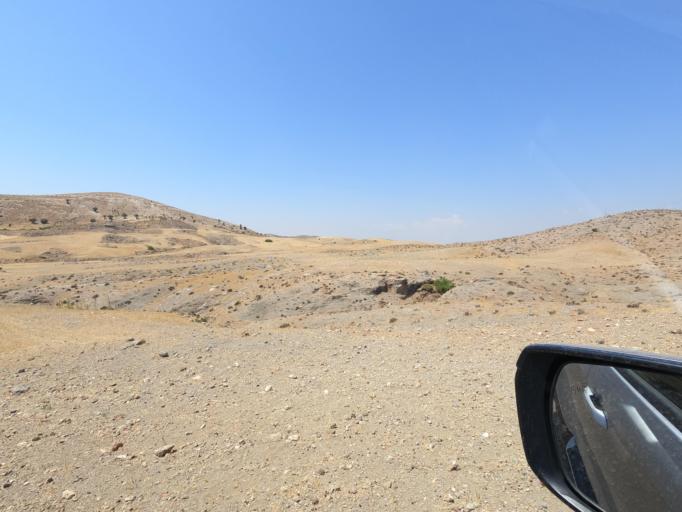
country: CY
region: Larnaka
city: Troulloi
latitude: 34.9996
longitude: 33.6171
